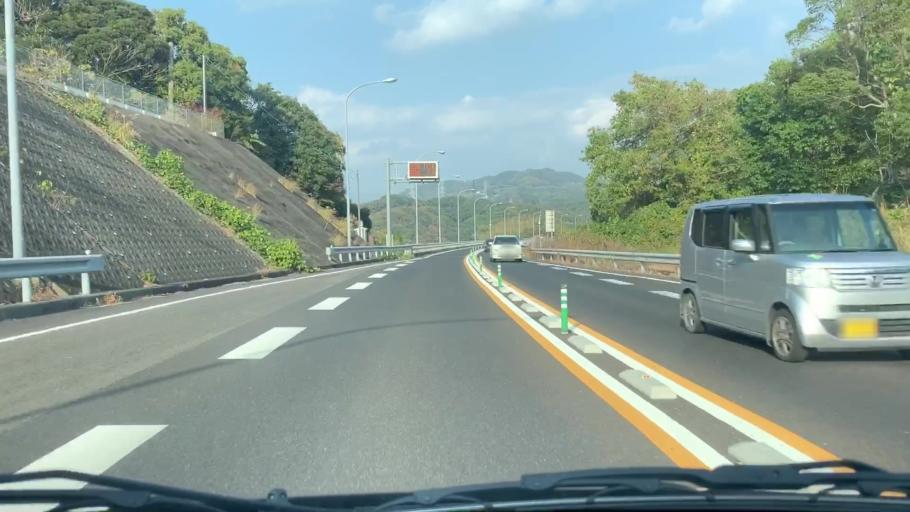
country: JP
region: Nagasaki
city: Sasebo
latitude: 33.0739
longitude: 129.7672
